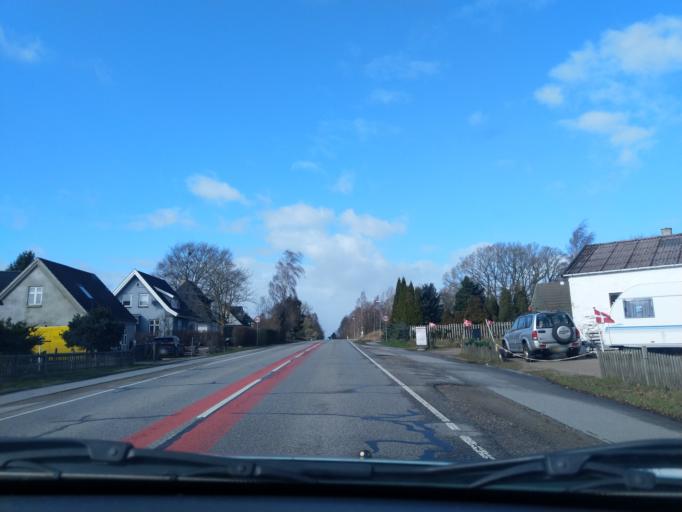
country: DK
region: Zealand
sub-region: Naestved Kommune
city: Naestved
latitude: 55.2664
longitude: 11.7461
